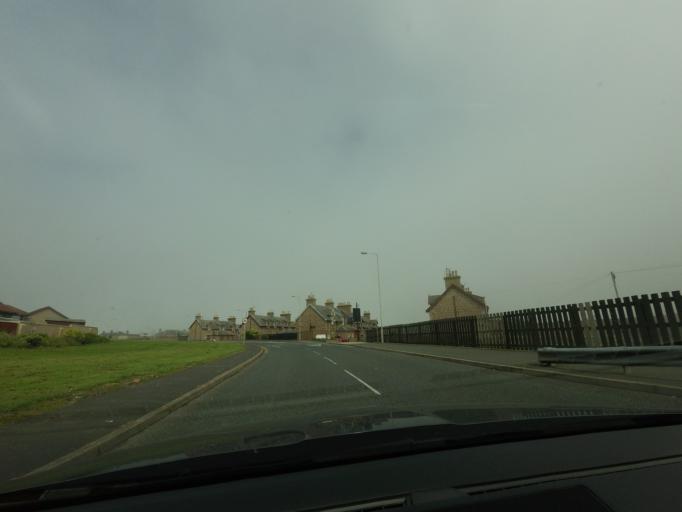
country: GB
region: Scotland
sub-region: Aberdeenshire
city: Peterhead
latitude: 57.4894
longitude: -1.7930
